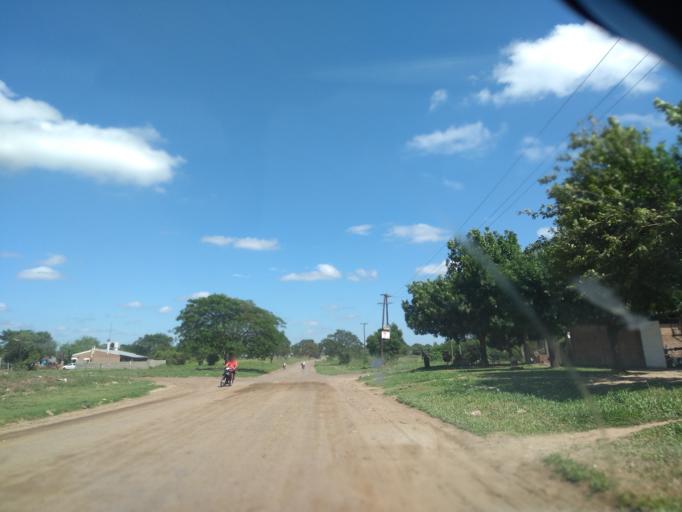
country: AR
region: Chaco
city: Fontana
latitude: -27.4060
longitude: -59.0374
